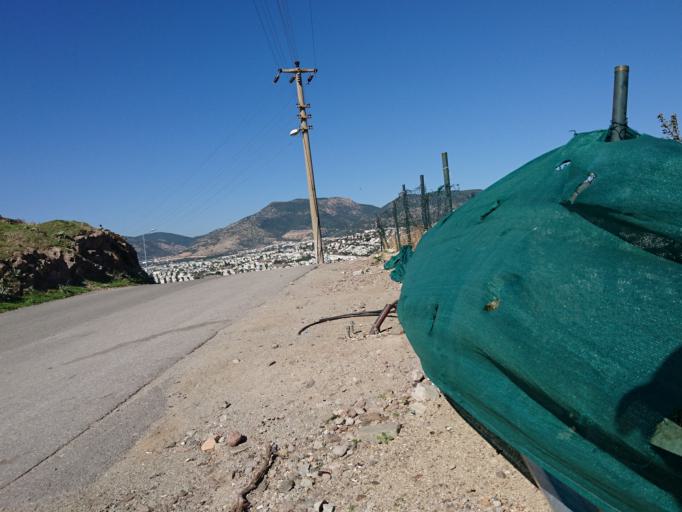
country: TR
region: Mugla
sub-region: Bodrum
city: Bodrum
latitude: 37.0264
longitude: 27.4147
